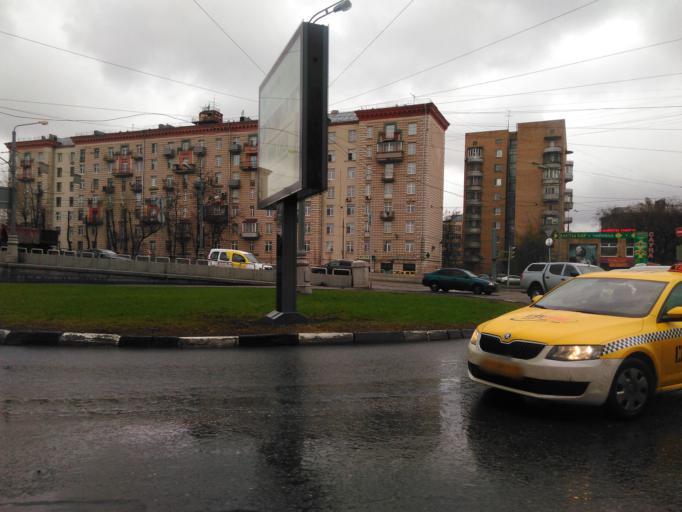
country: RU
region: Moscow
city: Taganskiy
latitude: 55.7278
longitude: 37.6508
